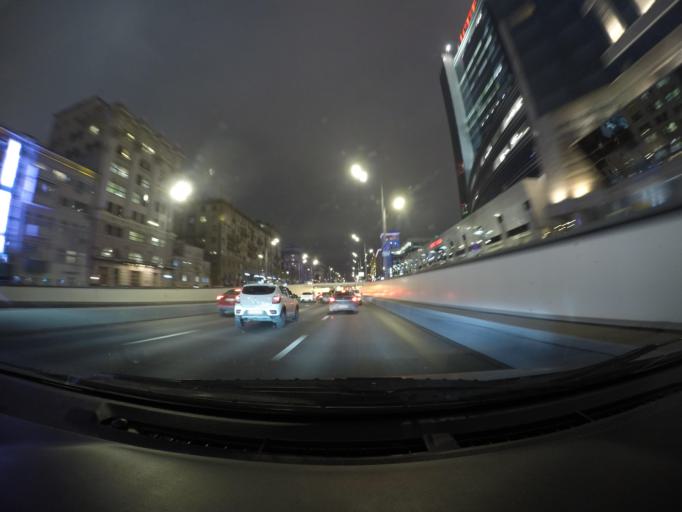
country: RU
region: Moskovskaya
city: Dorogomilovo
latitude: 55.7504
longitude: 37.5833
